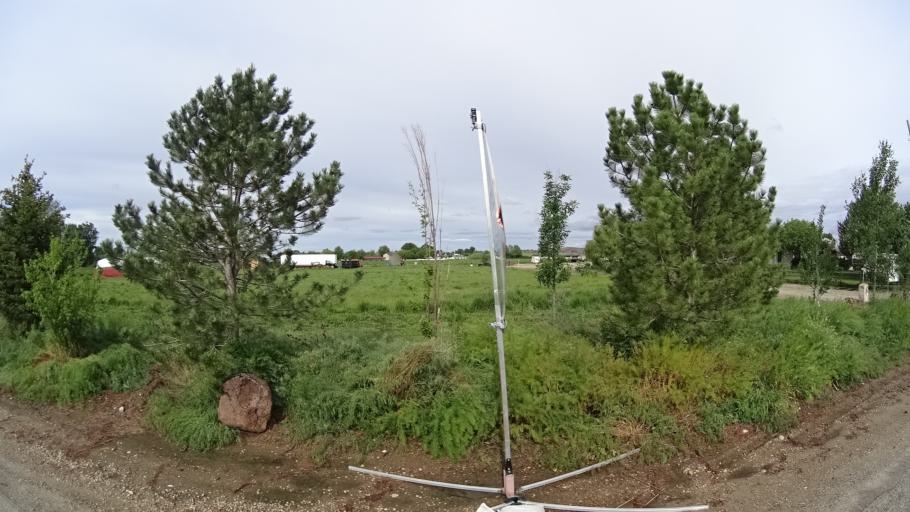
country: US
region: Idaho
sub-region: Ada County
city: Eagle
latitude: 43.7238
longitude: -116.4035
